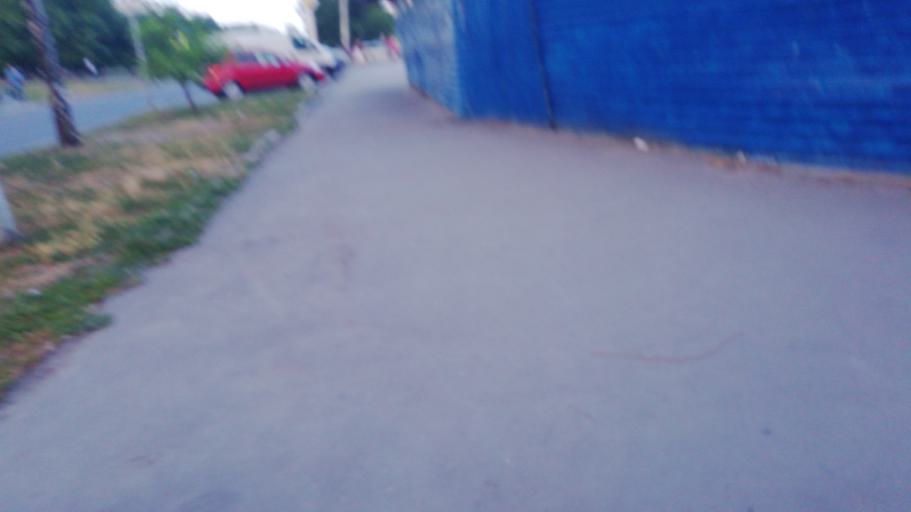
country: RU
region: Rostov
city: Severnyy
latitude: 47.2875
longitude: 39.7076
